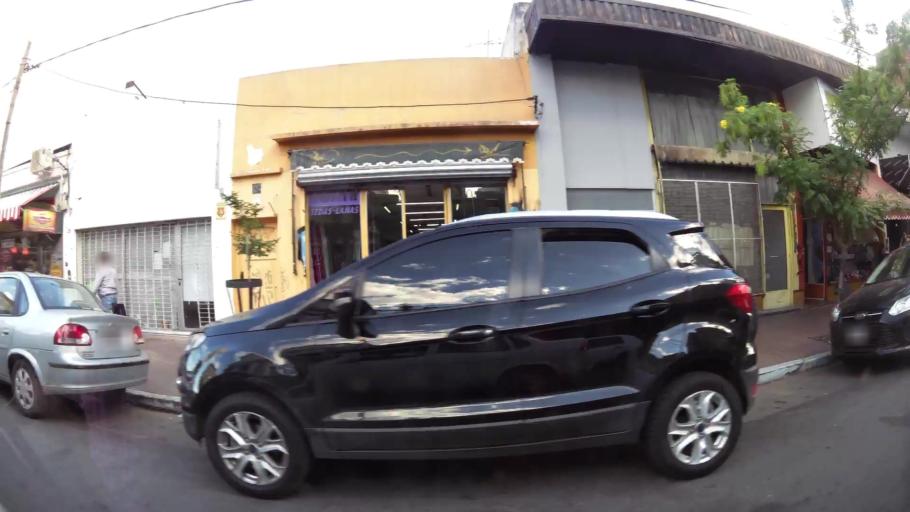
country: AR
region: Buenos Aires
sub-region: Partido de General San Martin
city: General San Martin
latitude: -34.5477
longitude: -58.5517
